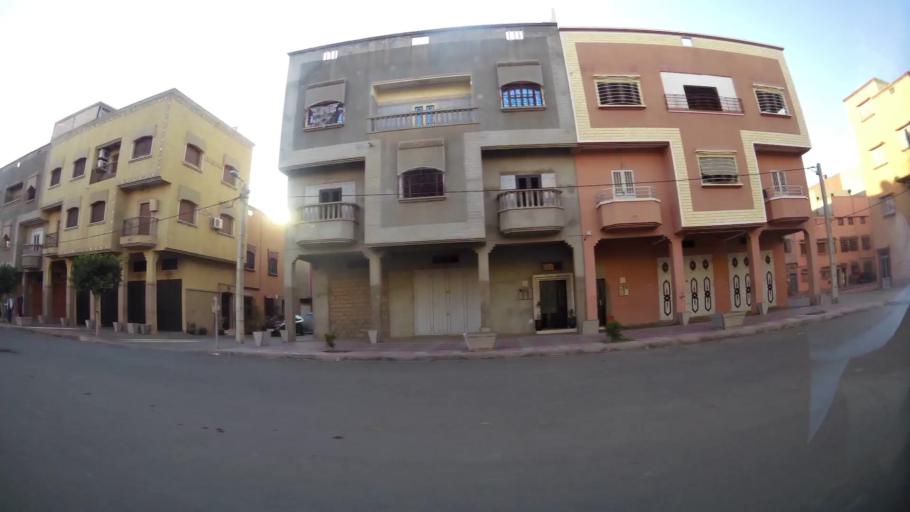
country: MA
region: Marrakech-Tensift-Al Haouz
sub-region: Kelaa-Des-Sraghna
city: Sidi Abdallah
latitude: 32.2397
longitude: -7.9620
